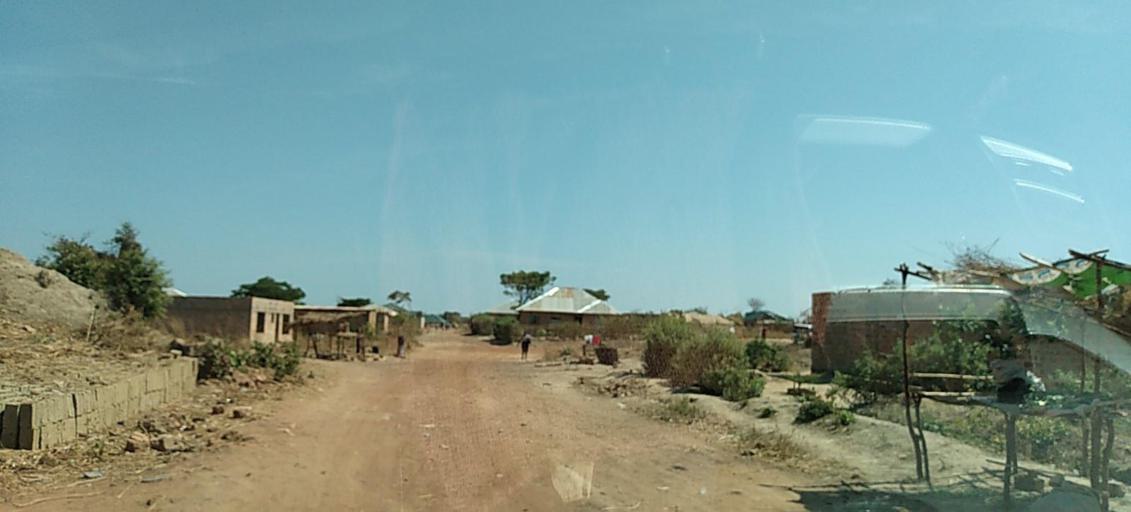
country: ZM
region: Copperbelt
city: Chililabombwe
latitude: -12.3215
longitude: 27.8603
